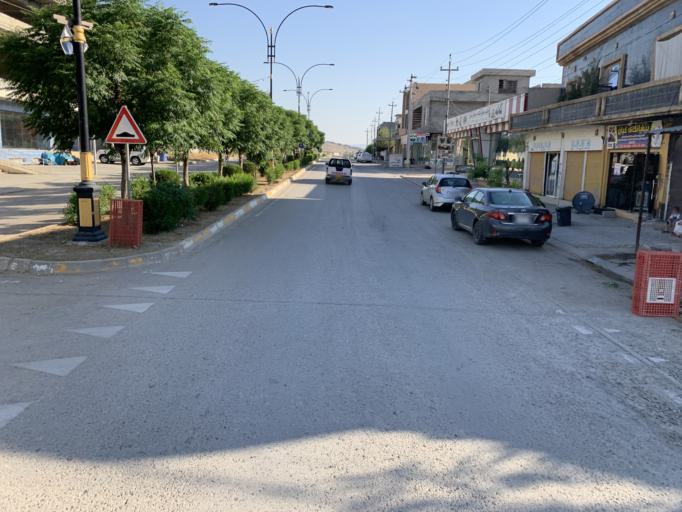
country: IQ
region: As Sulaymaniyah
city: Raniye
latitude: 36.2436
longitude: 44.8728
